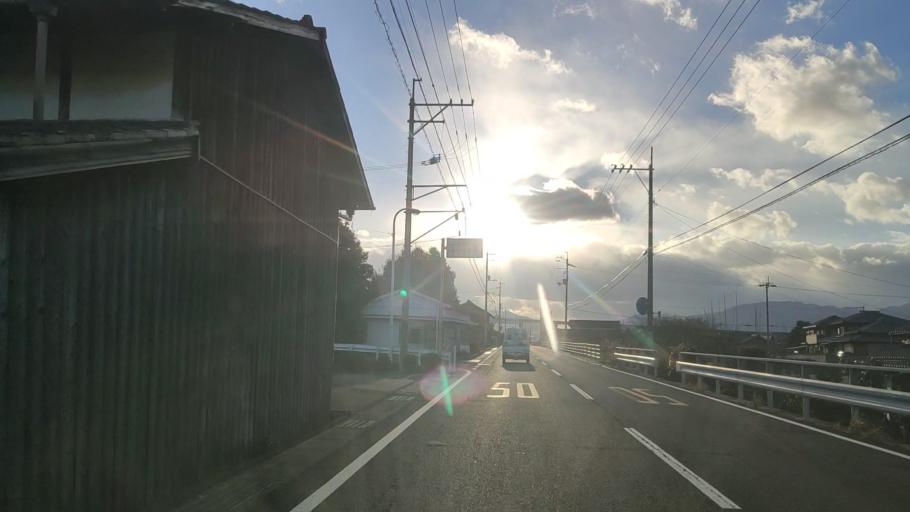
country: JP
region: Ehime
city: Saijo
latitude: 33.8928
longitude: 133.0918
